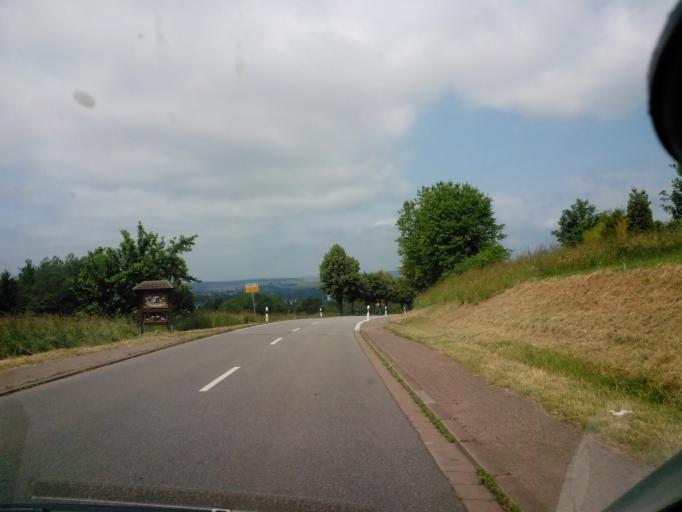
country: DE
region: Saarland
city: Eppelborn
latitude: 49.3973
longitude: 6.9844
